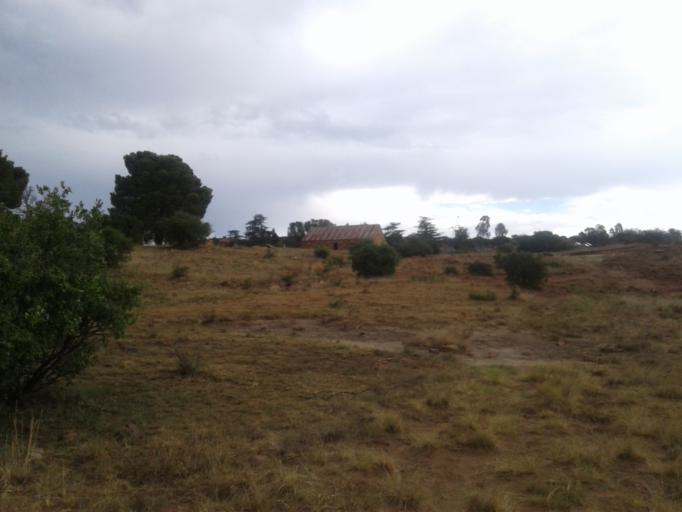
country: LS
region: Quthing
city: Quthing
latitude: -30.3841
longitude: 27.5608
